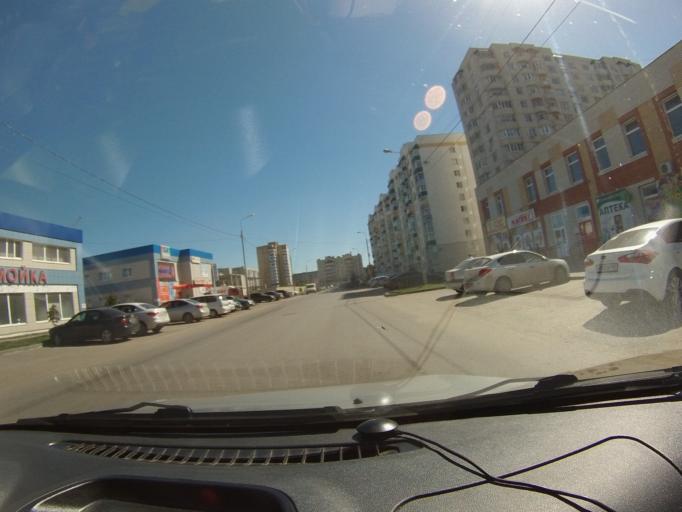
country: RU
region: Tambov
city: Tambov
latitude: 52.7711
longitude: 41.4037
